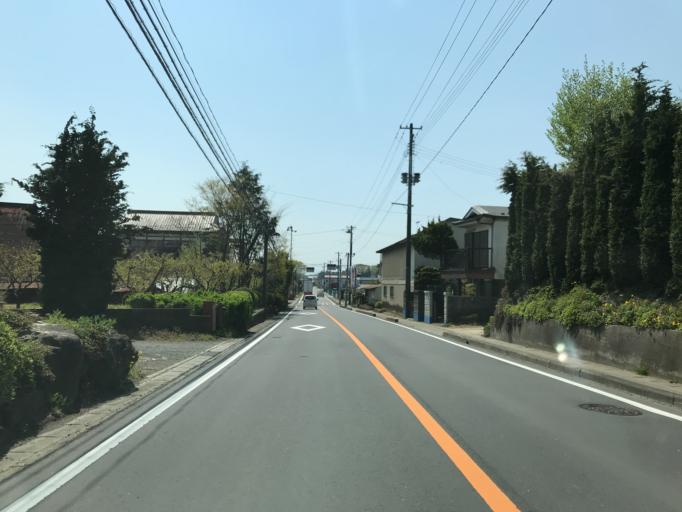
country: JP
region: Fukushima
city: Ishikawa
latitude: 37.1355
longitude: 140.3499
